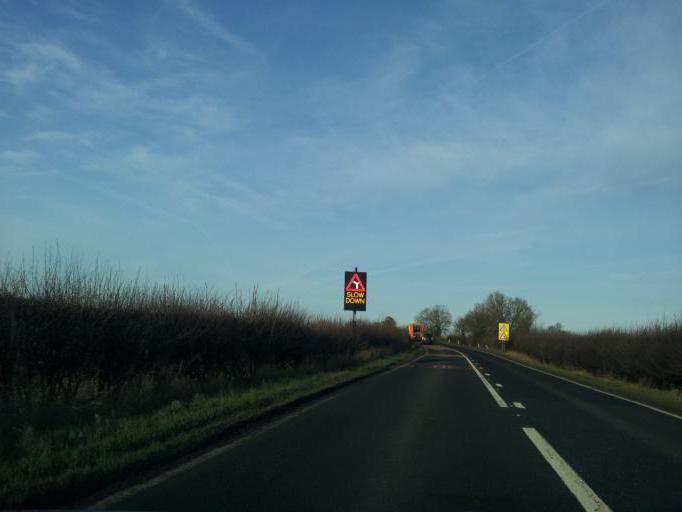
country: GB
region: England
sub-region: Nottinghamshire
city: Farndon
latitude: 53.0931
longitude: -0.8840
